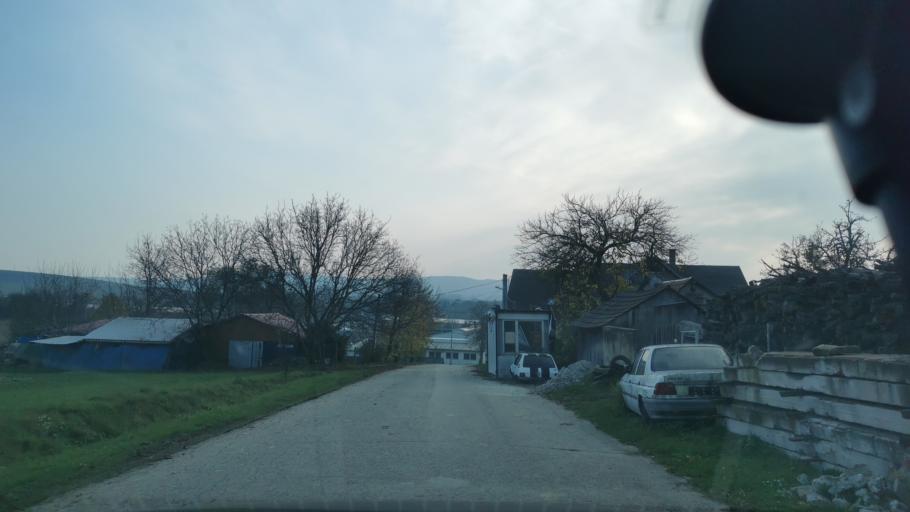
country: SK
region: Trnavsky
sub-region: Okres Skalica
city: Skalica
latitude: 48.7725
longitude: 17.2866
